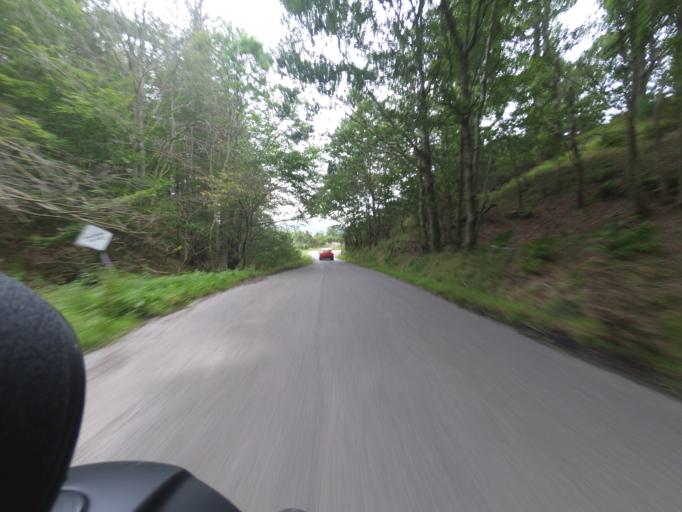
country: GB
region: Scotland
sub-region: Highland
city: Inverness
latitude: 57.5096
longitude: -4.2619
